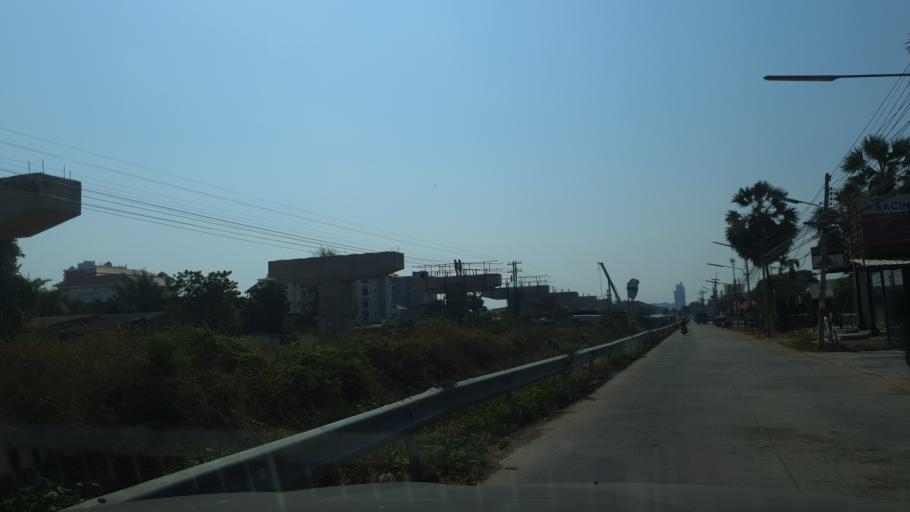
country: TH
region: Prachuap Khiri Khan
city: Hua Hin
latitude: 12.5562
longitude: 99.9572
